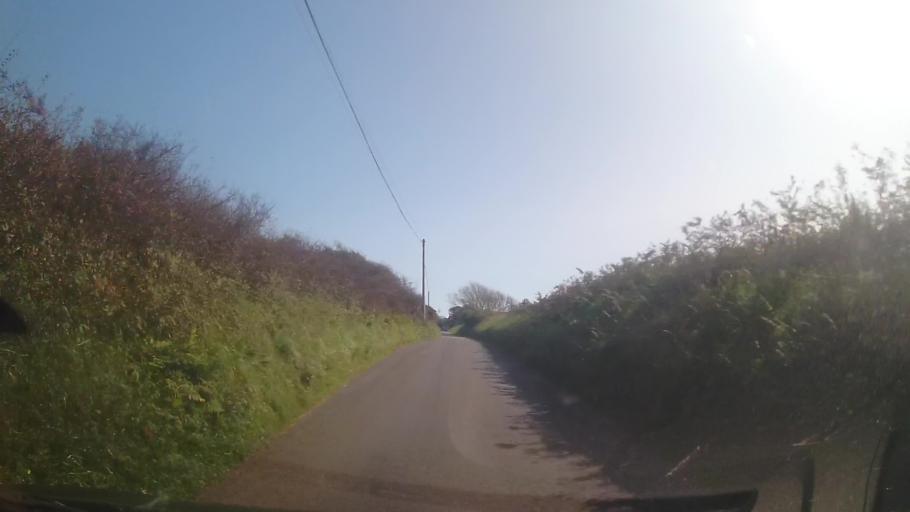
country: GB
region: Wales
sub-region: Pembrokeshire
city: Llanrhian
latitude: 51.9308
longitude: -5.1634
